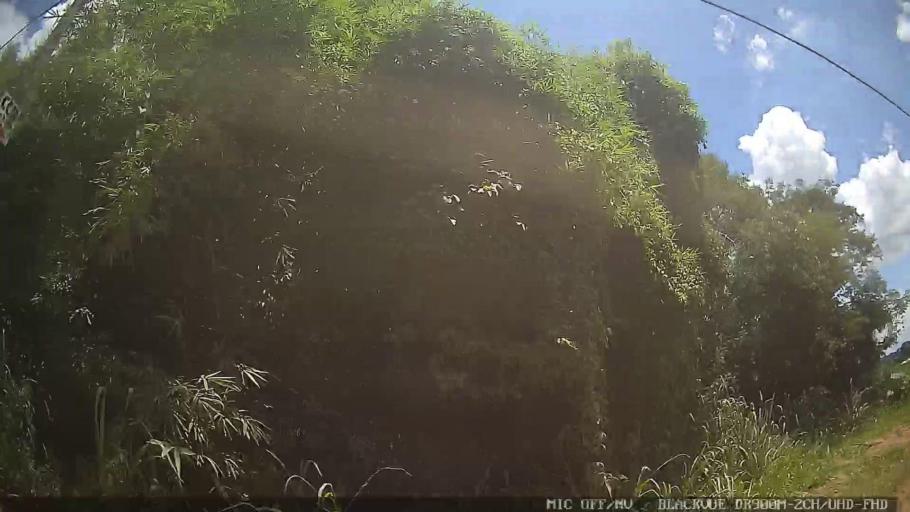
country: BR
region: Sao Paulo
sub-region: Atibaia
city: Atibaia
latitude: -23.1248
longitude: -46.6279
